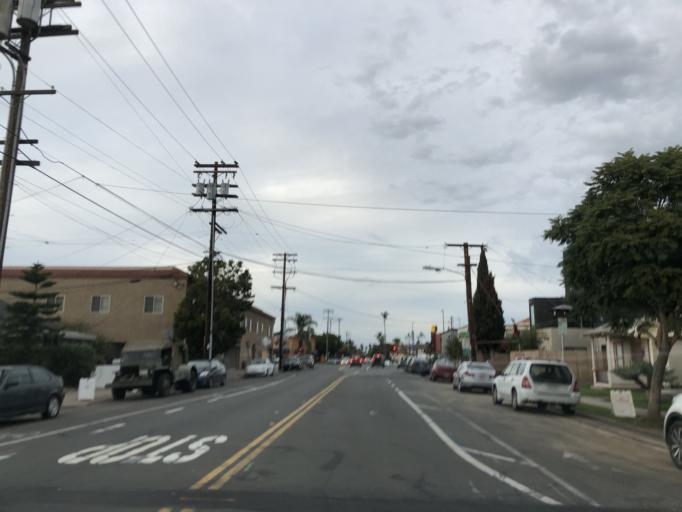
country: US
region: California
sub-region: San Diego County
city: San Diego
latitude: 32.7475
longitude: -117.1512
